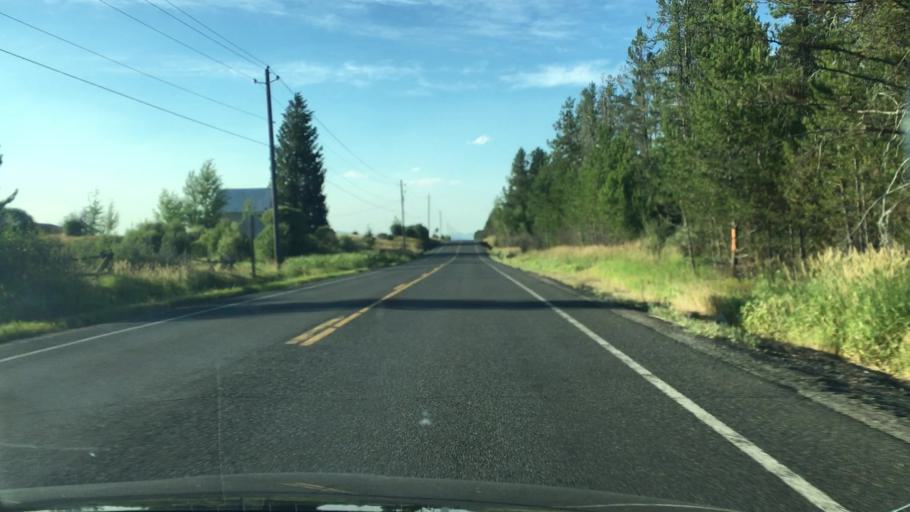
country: US
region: Idaho
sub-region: Valley County
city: McCall
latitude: 44.7930
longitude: -116.0782
